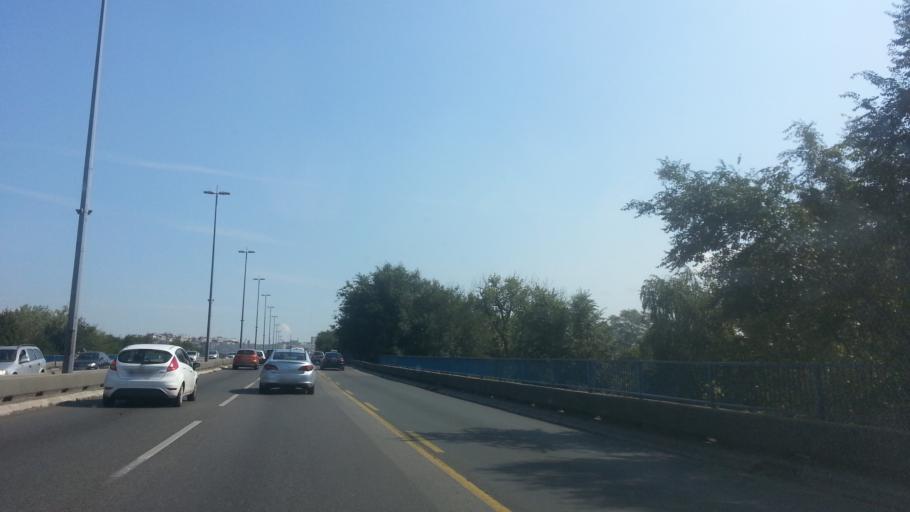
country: RS
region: Central Serbia
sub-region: Belgrade
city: Stari Grad
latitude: 44.8145
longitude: 20.4421
